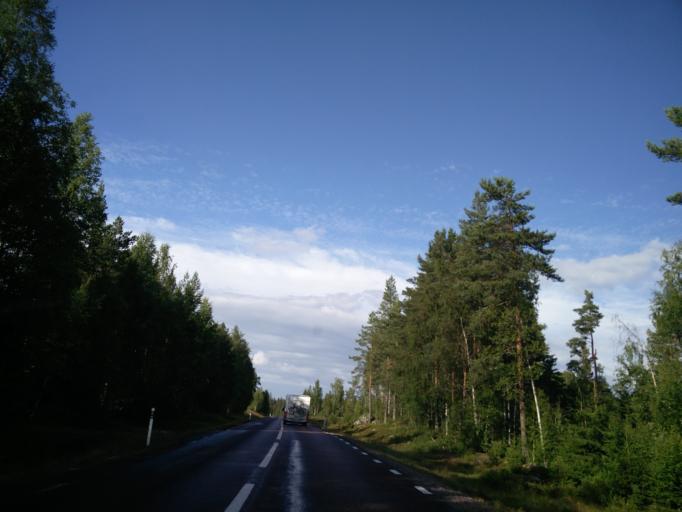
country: SE
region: Vaermland
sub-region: Hagfors Kommun
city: Ekshaerad
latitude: 60.4858
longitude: 13.4085
